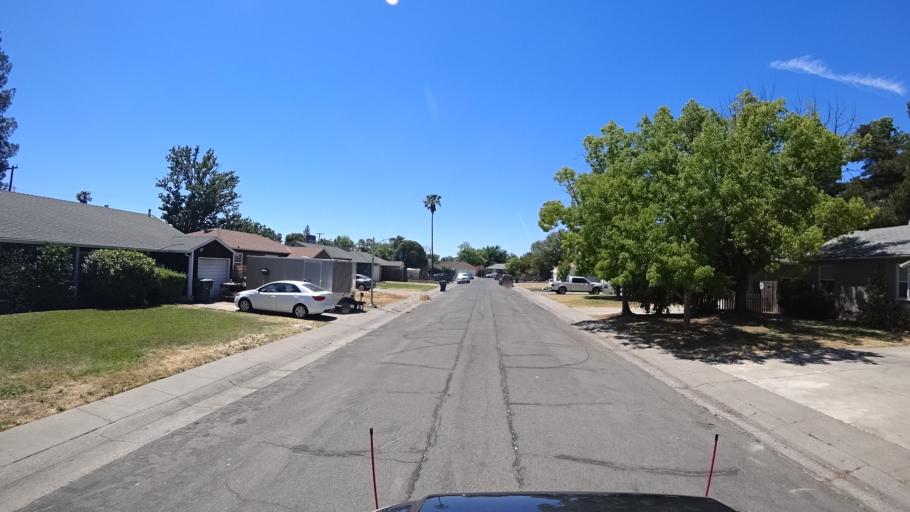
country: US
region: California
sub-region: Sacramento County
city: Florin
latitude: 38.5212
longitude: -121.4296
